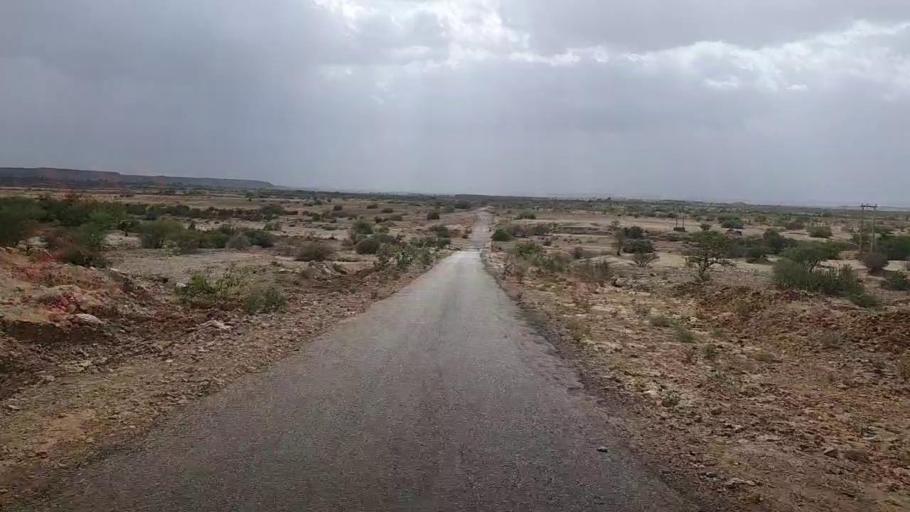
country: PK
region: Sindh
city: Jamshoro
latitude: 25.3940
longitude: 67.7307
